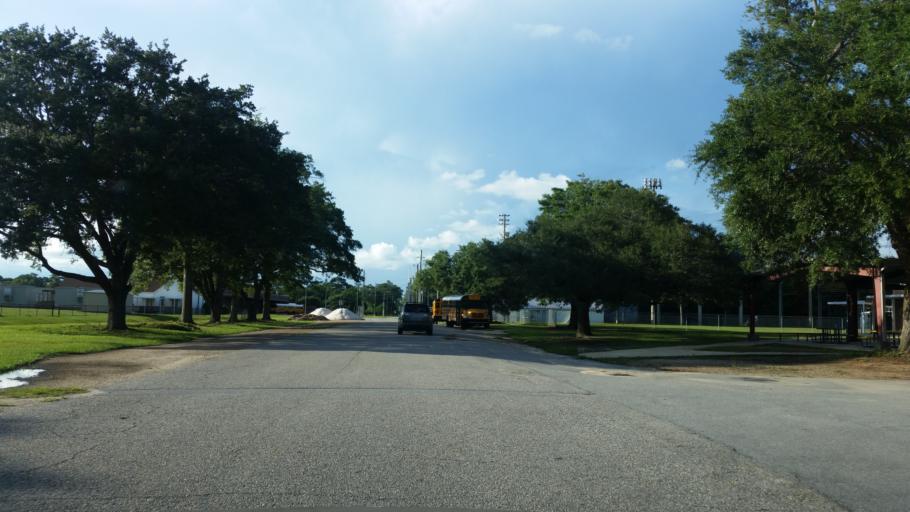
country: US
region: Alabama
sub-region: Baldwin County
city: Foley
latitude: 30.4074
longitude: -87.6894
